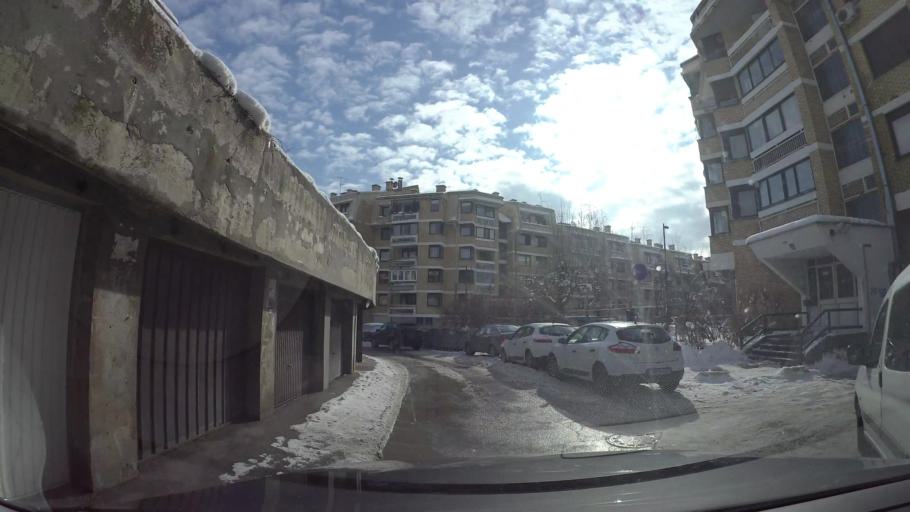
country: BA
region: Federation of Bosnia and Herzegovina
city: Kobilja Glava
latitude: 43.8723
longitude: 18.4190
